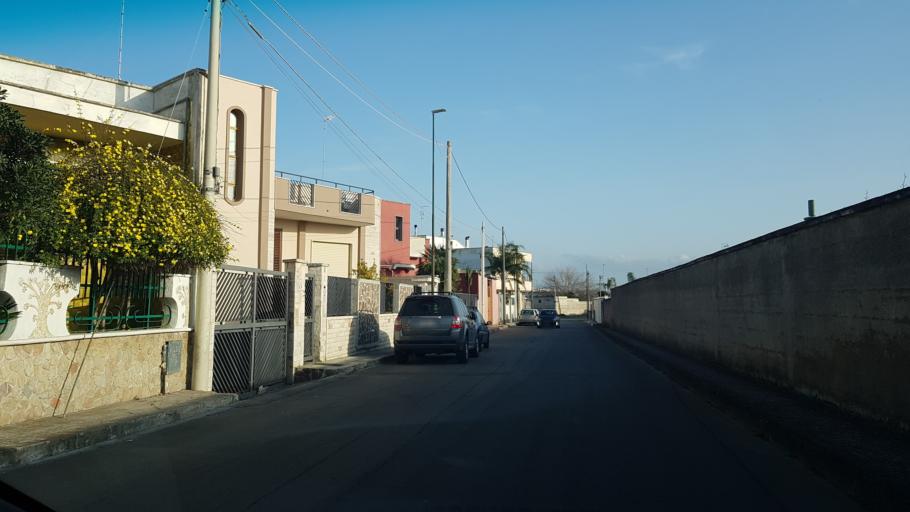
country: IT
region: Apulia
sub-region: Provincia di Lecce
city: Trepuzzi
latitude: 40.4063
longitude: 18.0647
